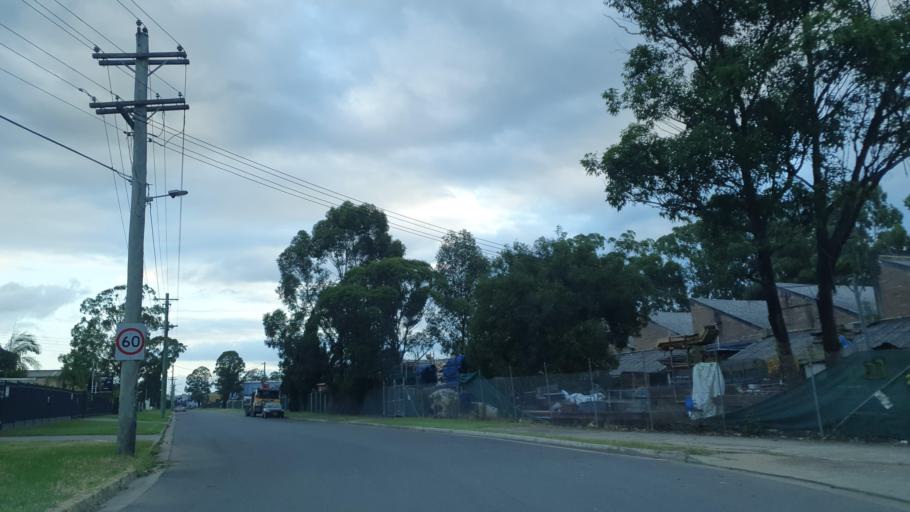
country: AU
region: New South Wales
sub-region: Penrith Municipality
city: Werrington County
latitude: -33.7416
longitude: 150.7693
